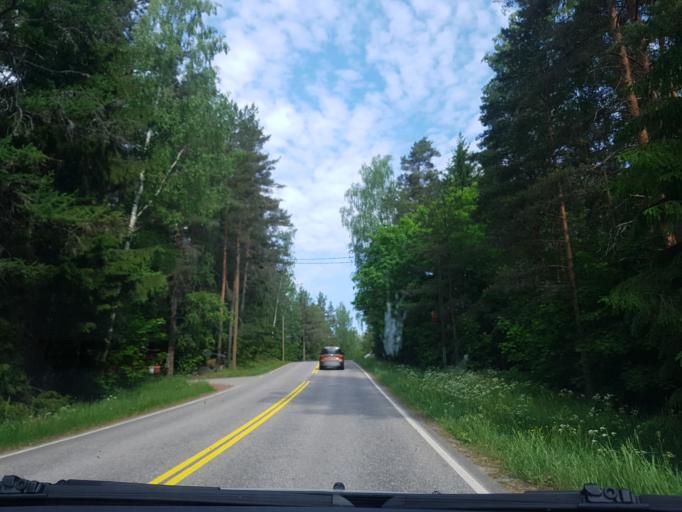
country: FI
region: Uusimaa
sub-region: Helsinki
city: Vihti
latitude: 60.3050
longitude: 24.3999
